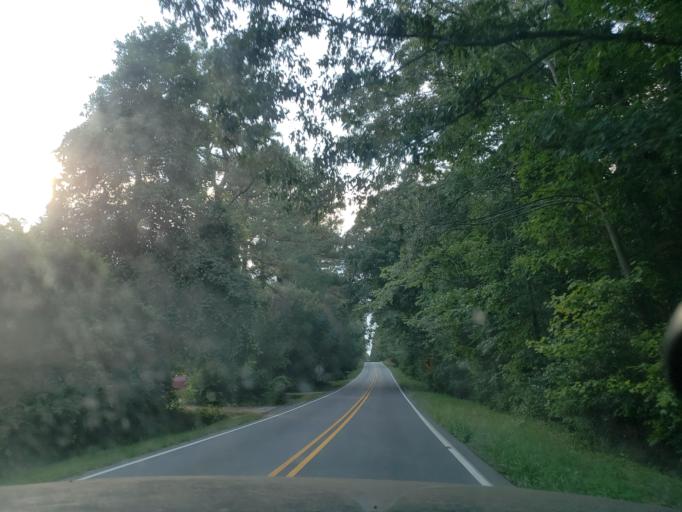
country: US
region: North Carolina
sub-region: Durham County
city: Durham
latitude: 35.9884
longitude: -78.9660
